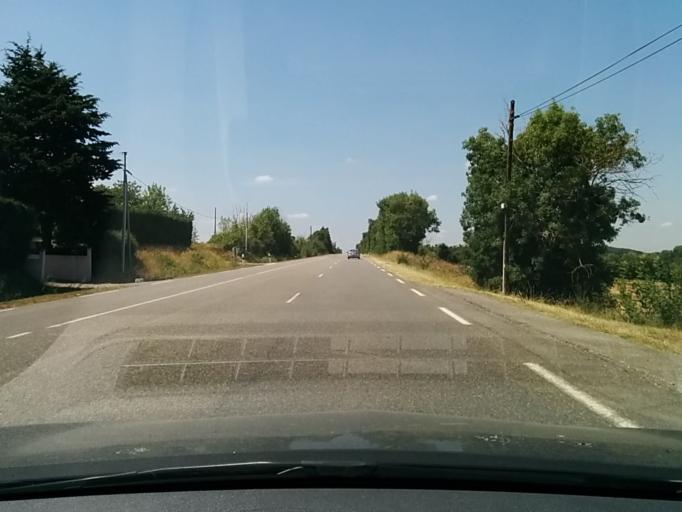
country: FR
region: Midi-Pyrenees
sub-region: Departement du Gers
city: Gimont
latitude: 43.6346
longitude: 0.8476
